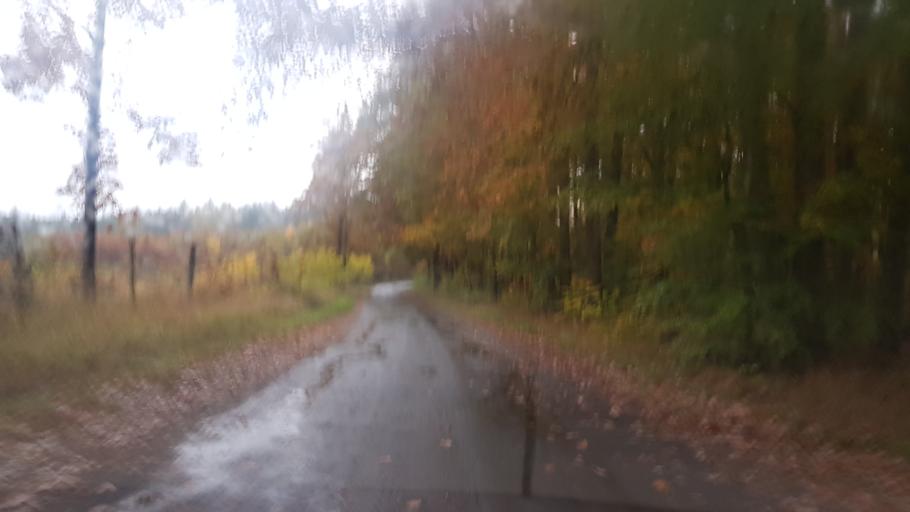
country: PL
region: West Pomeranian Voivodeship
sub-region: Powiat gryfinski
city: Chojna
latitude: 53.0419
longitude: 14.4652
